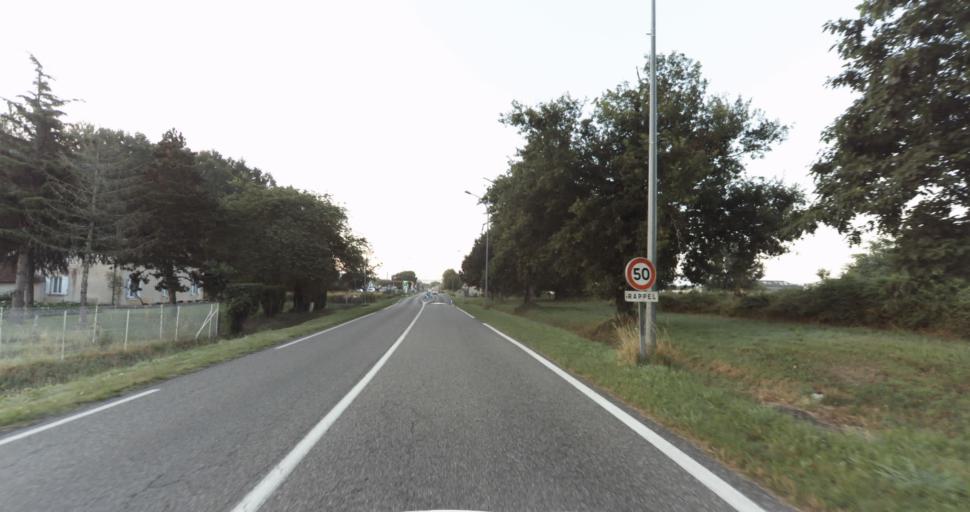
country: FR
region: Aquitaine
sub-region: Departement de la Gironde
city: Bazas
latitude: 44.4420
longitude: -0.2339
